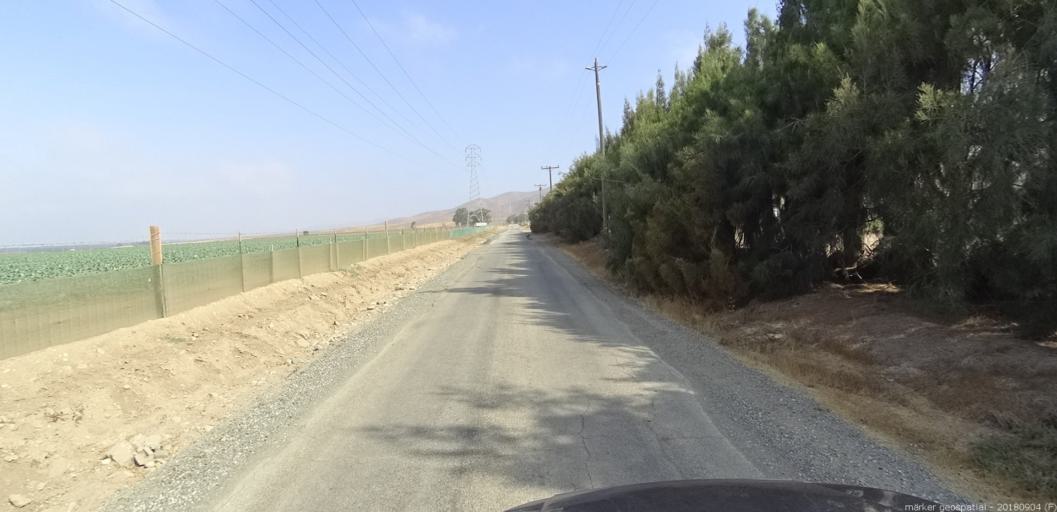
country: US
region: California
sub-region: Monterey County
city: Soledad
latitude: 36.4587
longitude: -121.3317
